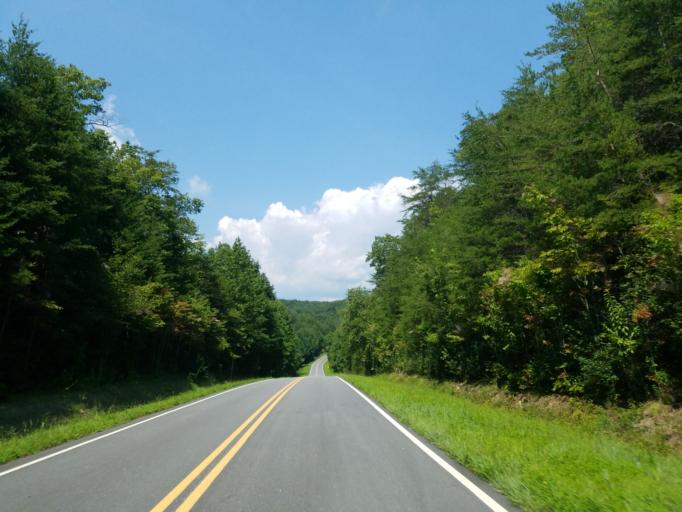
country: US
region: Georgia
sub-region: Lumpkin County
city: Dahlonega
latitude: 34.6173
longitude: -83.8991
